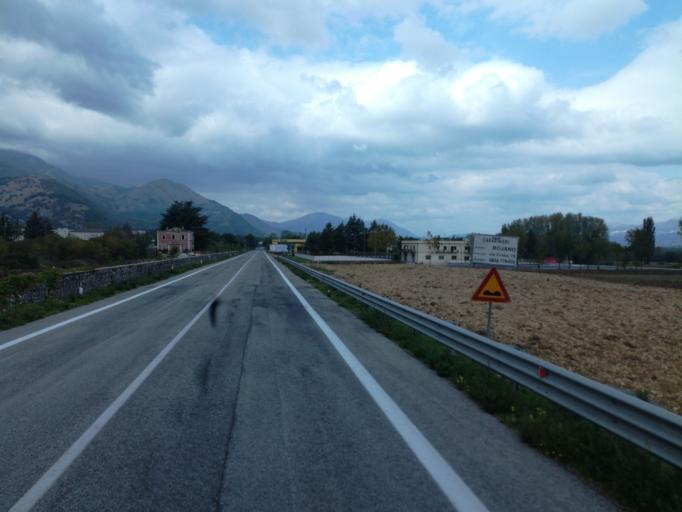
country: IT
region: Molise
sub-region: Provincia di Campobasso
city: Campochiaro
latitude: 41.4735
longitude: 14.5225
